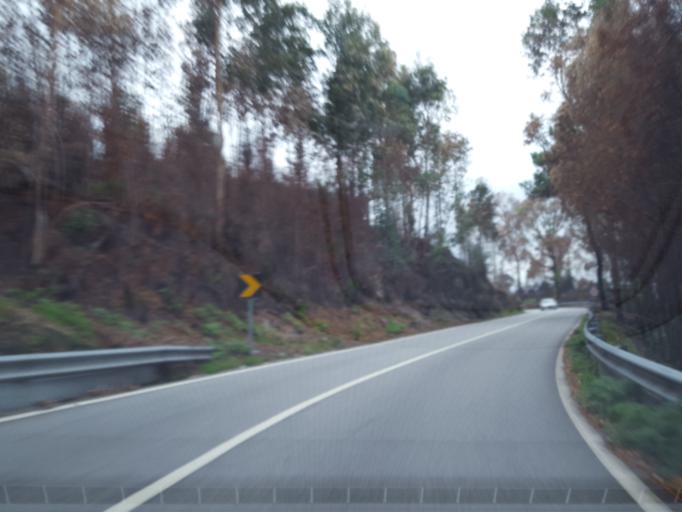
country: PT
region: Porto
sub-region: Marco de Canaveses
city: Marco de Canavezes
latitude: 41.1491
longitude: -8.1326
